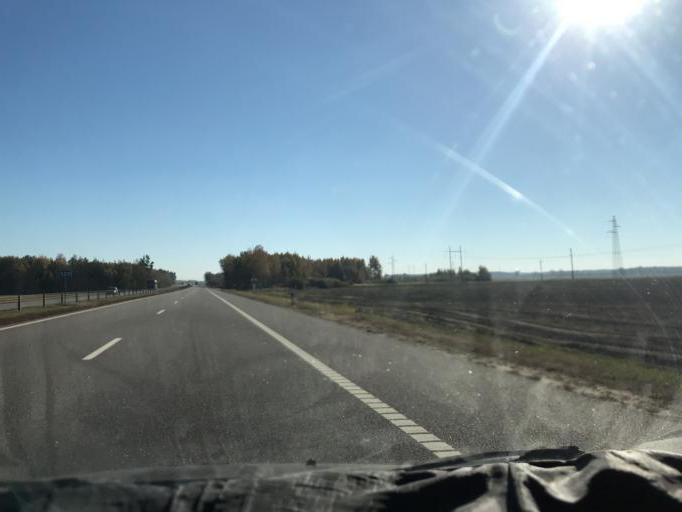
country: BY
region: Mogilev
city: Yalizava
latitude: 53.2275
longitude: 28.9994
